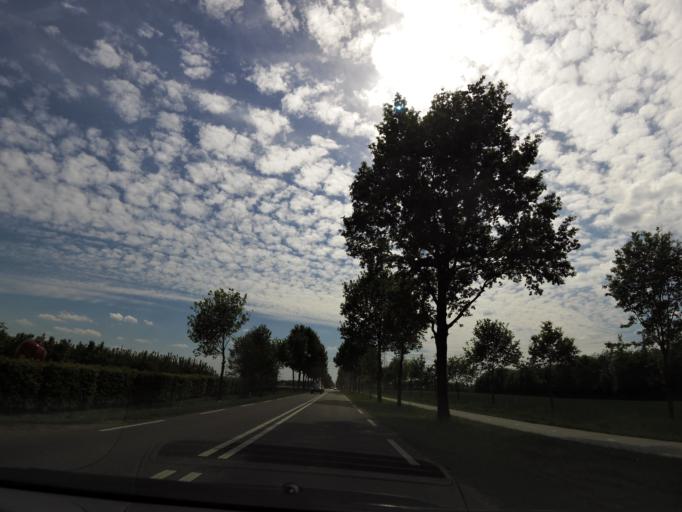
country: NL
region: Limburg
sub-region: Gemeente Leudal
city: Haelen
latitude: 51.2510
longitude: 5.9763
